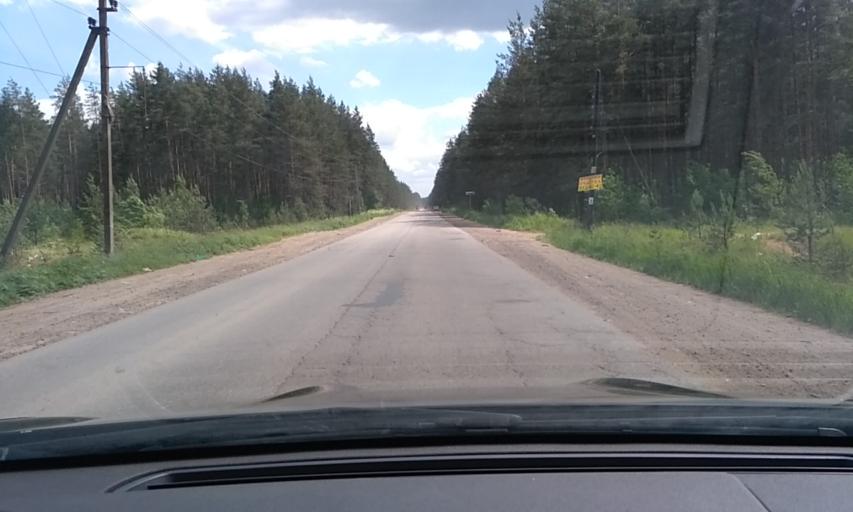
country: RU
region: Leningrad
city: Imeni Sverdlova
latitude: 59.8555
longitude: 30.6742
